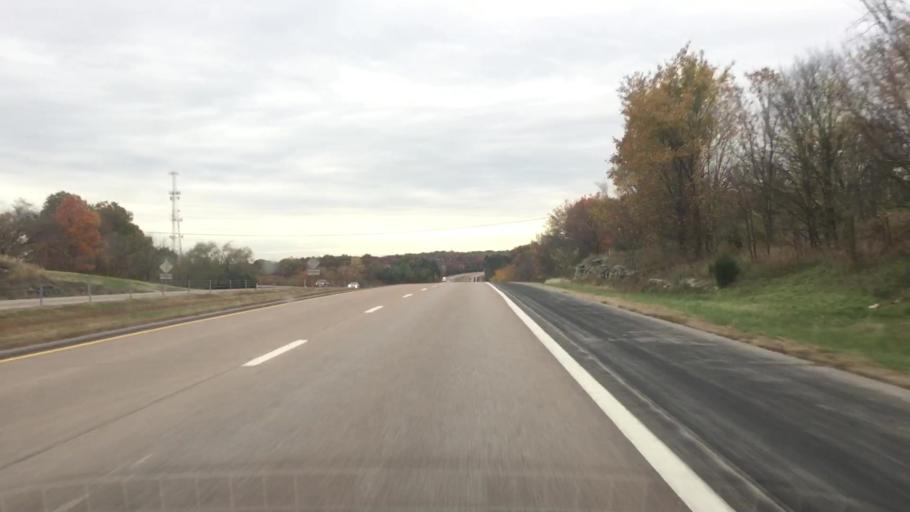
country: US
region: Missouri
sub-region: Boone County
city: Ashland
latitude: 38.6739
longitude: -92.2407
